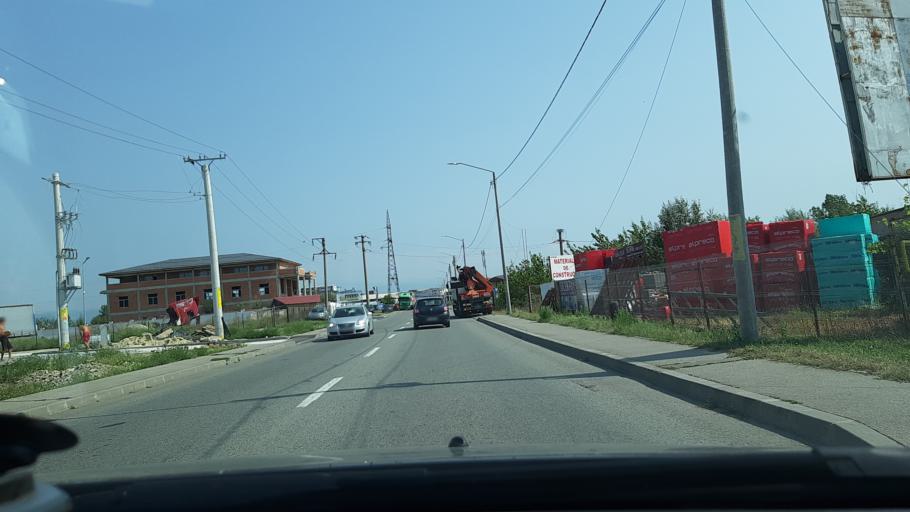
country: RO
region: Gorj
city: Targu Jiu
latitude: 45.0193
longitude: 23.2612
